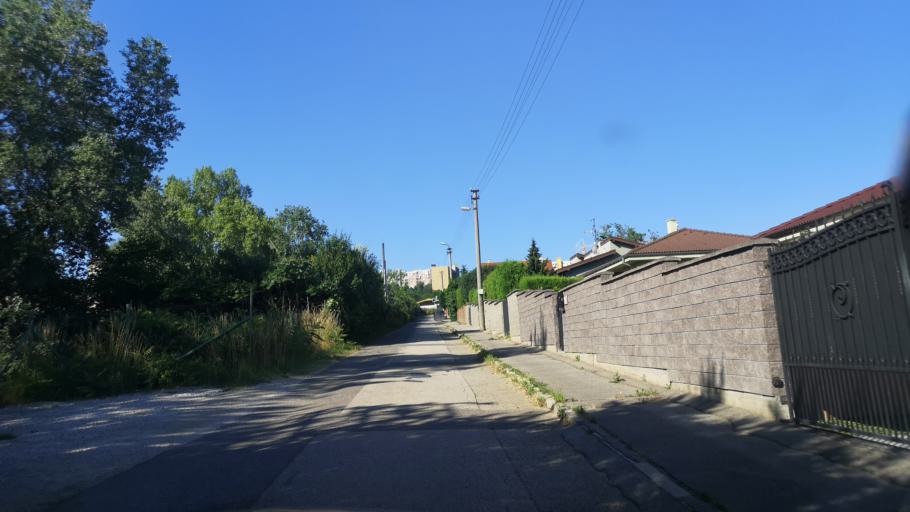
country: SK
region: Nitriansky
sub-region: Okres Nitra
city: Nitra
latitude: 48.3110
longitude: 18.0552
